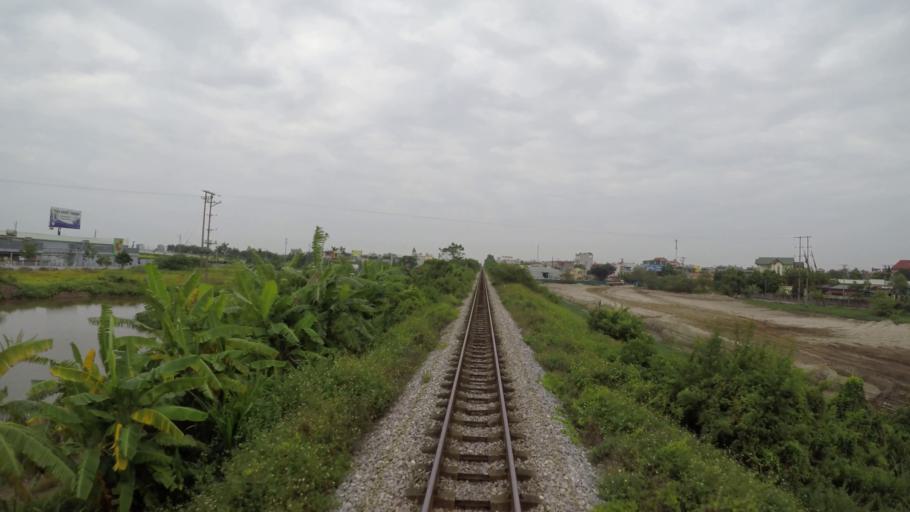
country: VN
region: Hai Duong
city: Thanh Pho Hai Duong
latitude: 20.9476
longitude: 106.3616
